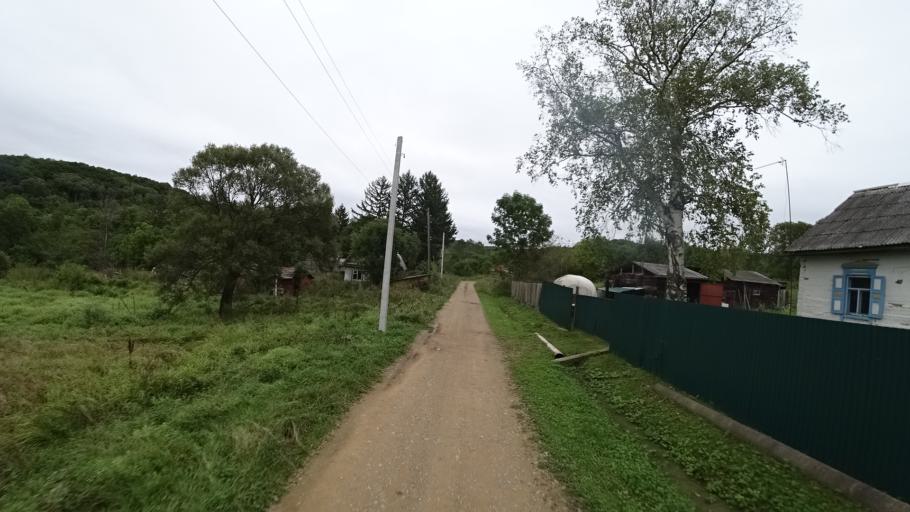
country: RU
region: Primorskiy
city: Rettikhovka
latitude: 44.1749
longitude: 132.8877
